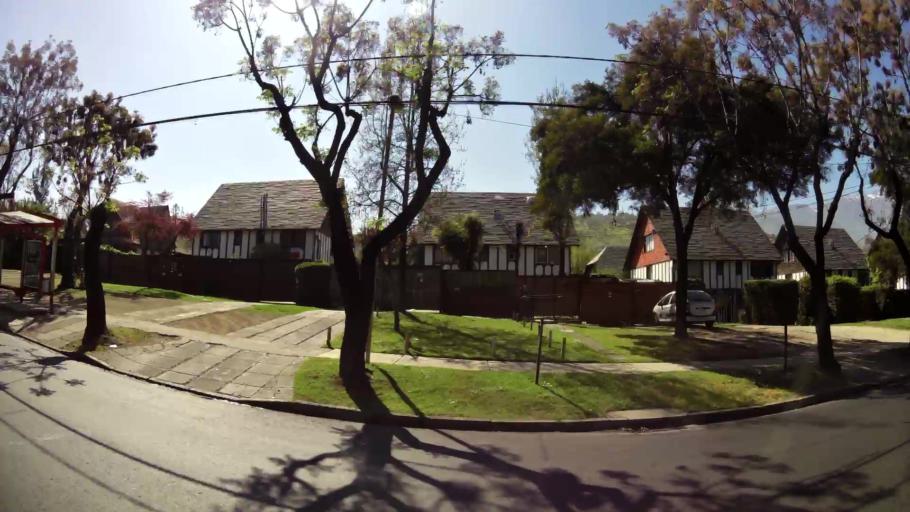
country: CL
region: Santiago Metropolitan
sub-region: Provincia de Santiago
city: Villa Presidente Frei, Nunoa, Santiago, Chile
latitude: -33.4082
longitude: -70.5370
